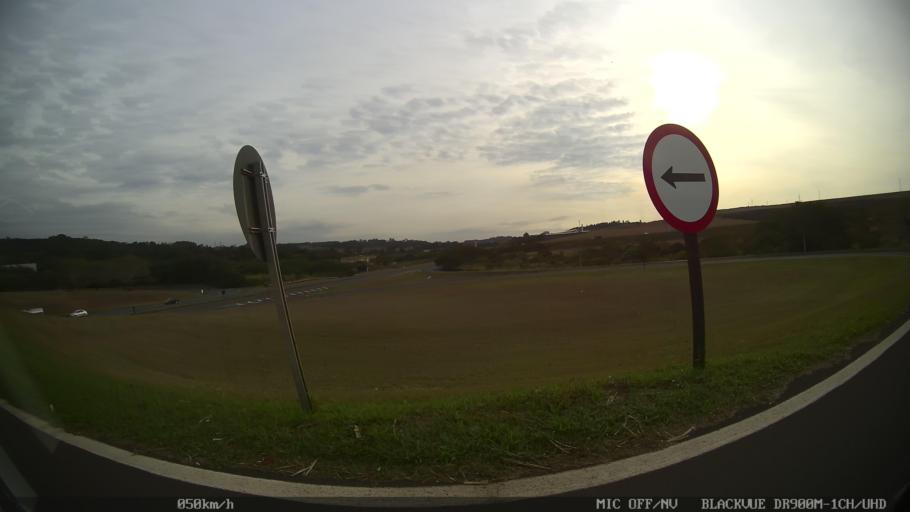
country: BR
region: Sao Paulo
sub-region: Piracicaba
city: Piracicaba
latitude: -22.6989
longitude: -47.6024
